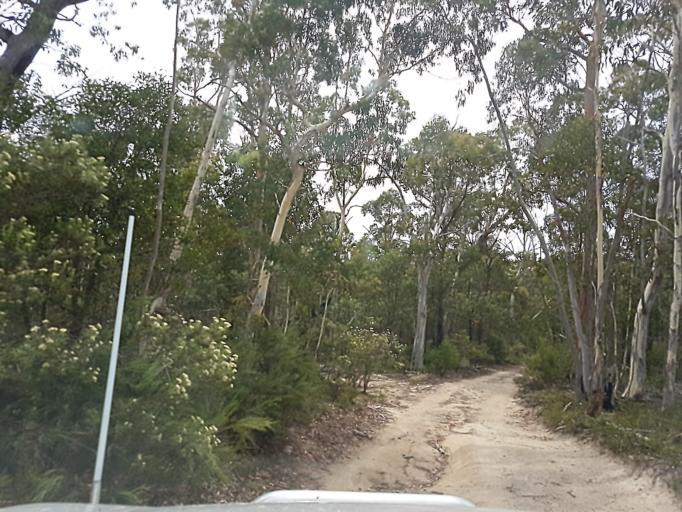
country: AU
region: New South Wales
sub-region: Snowy River
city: Jindabyne
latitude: -36.8284
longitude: 148.2190
